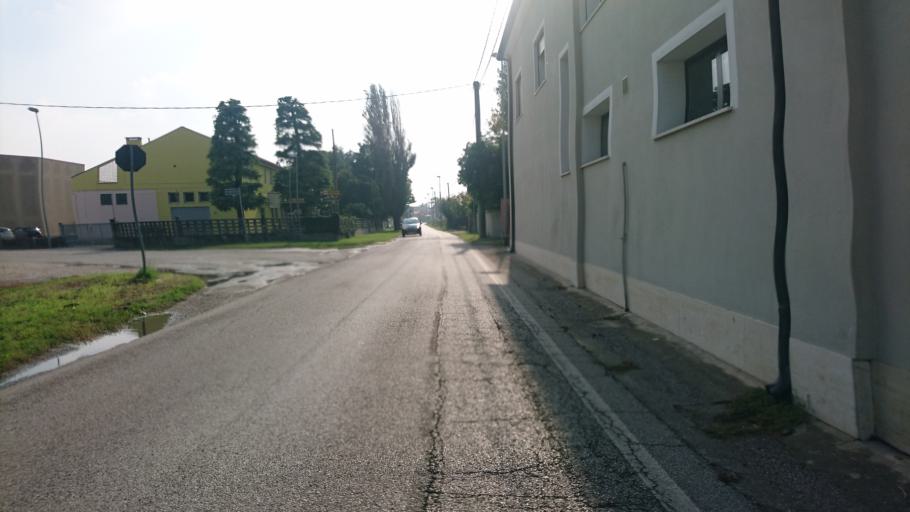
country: IT
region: Veneto
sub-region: Provincia di Rovigo
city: Rovigo
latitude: 45.0556
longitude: 11.7779
